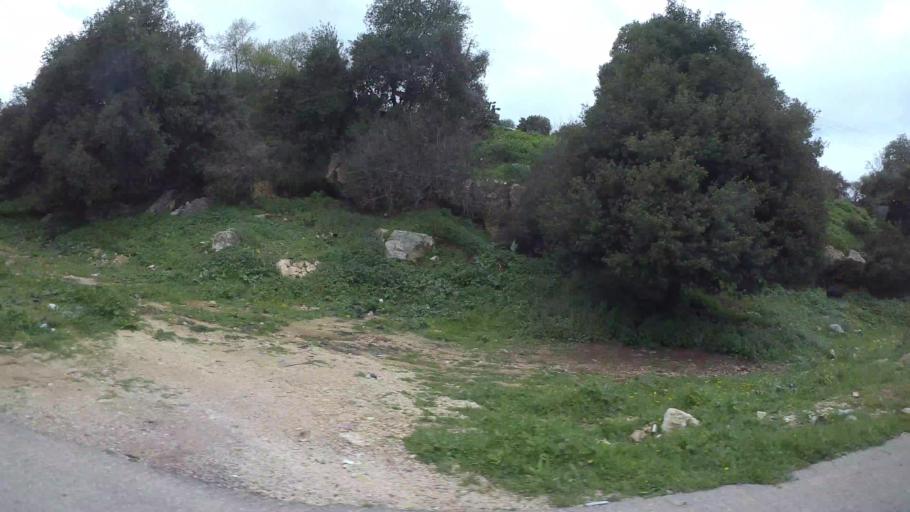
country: JO
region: Amman
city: Wadi as Sir
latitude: 31.9539
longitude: 35.8132
